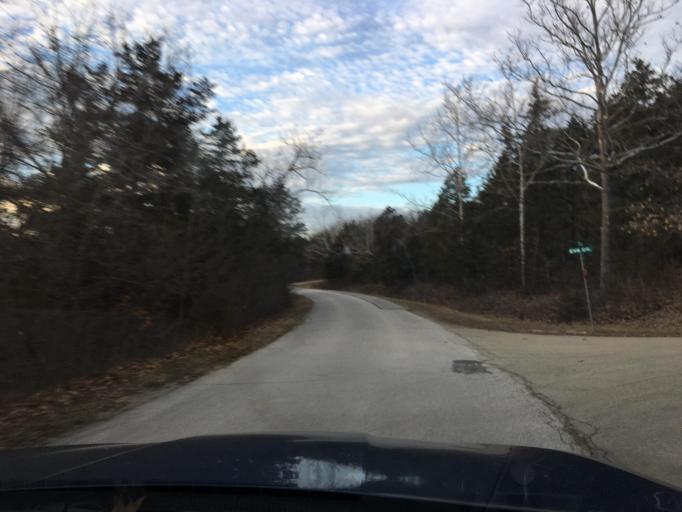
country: US
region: Missouri
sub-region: Jefferson County
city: De Soto
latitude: 38.0940
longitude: -90.5659
